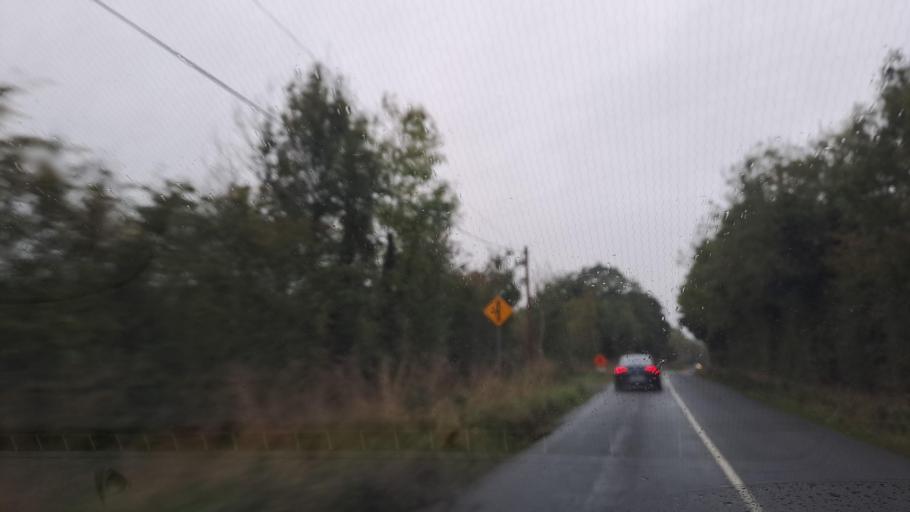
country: IE
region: Ulster
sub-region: County Monaghan
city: Monaghan
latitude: 54.2221
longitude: -6.9268
